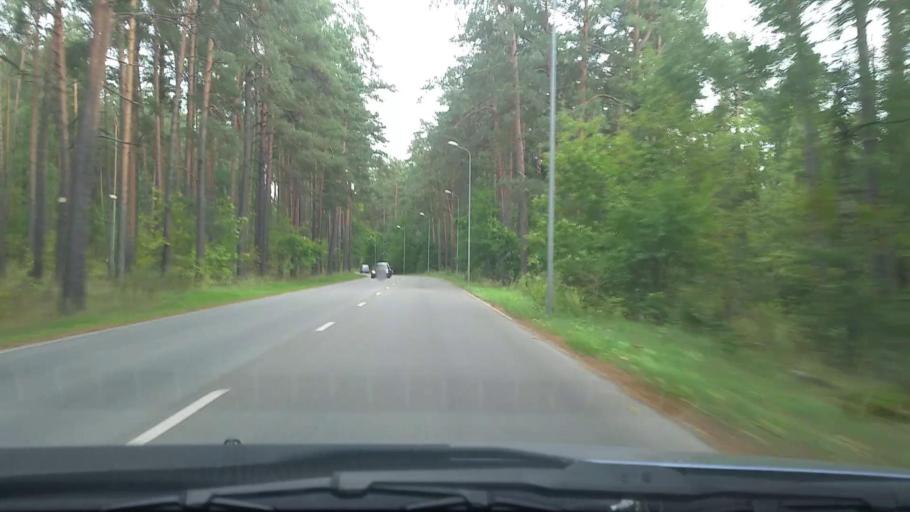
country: LV
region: Riga
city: Jaunciems
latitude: 56.9794
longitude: 24.2138
